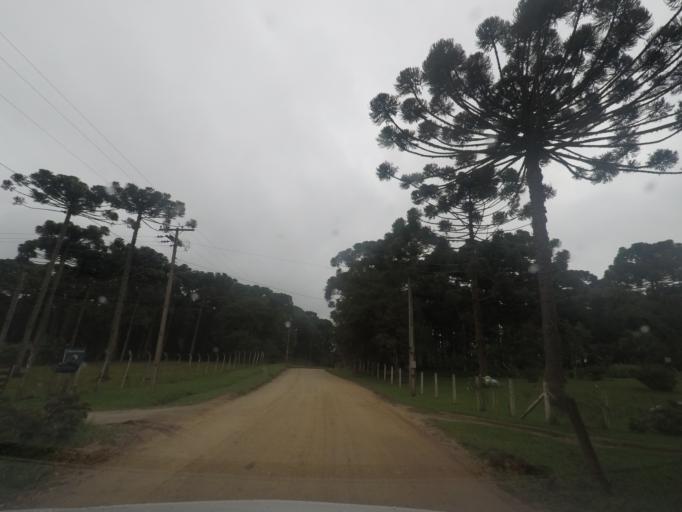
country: BR
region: Parana
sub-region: Campina Grande Do Sul
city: Campina Grande do Sul
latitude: -25.3087
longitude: -49.0992
